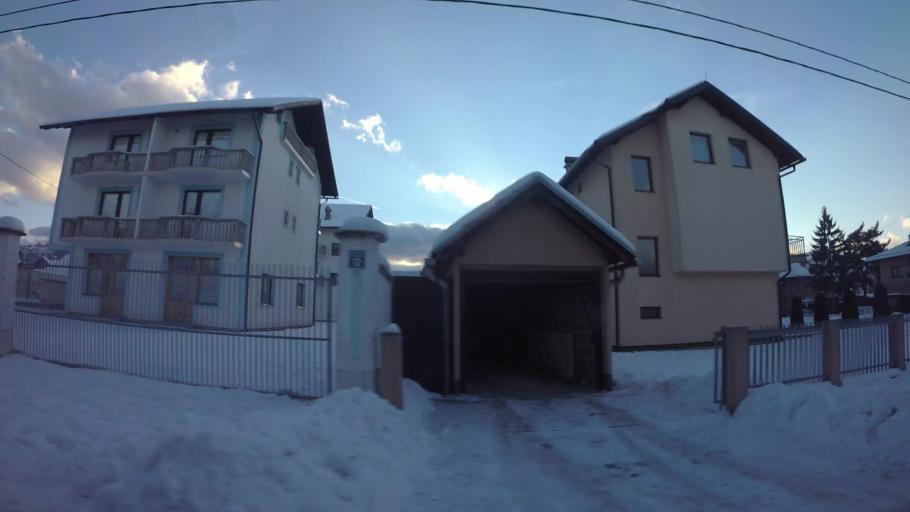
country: BA
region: Federation of Bosnia and Herzegovina
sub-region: Kanton Sarajevo
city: Sarajevo
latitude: 43.8150
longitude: 18.3553
